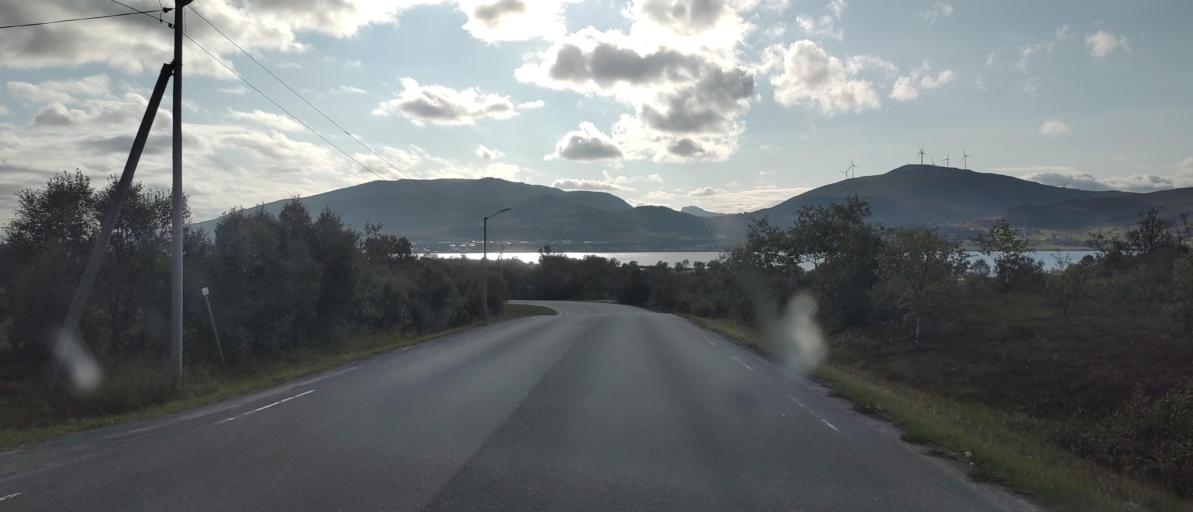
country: NO
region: Nordland
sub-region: Sortland
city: Sortland
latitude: 68.7201
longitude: 15.4613
